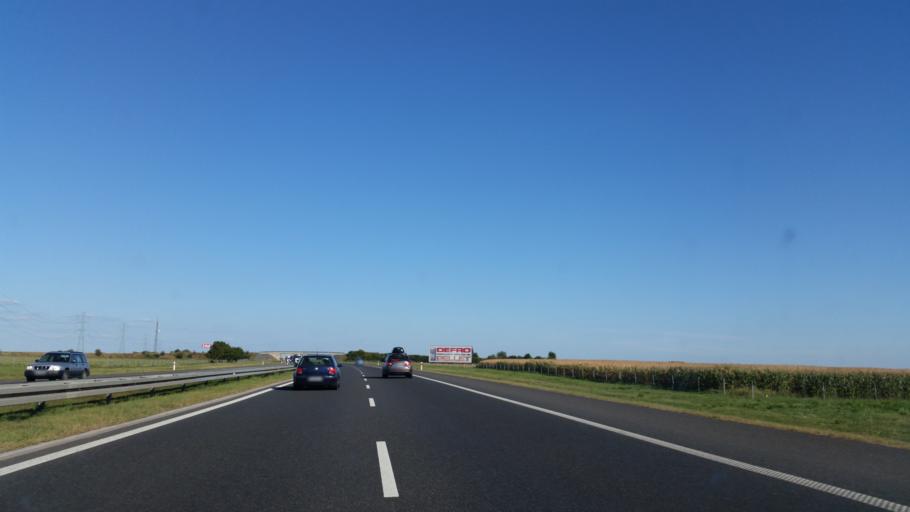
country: PL
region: Opole Voivodeship
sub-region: Powiat brzeski
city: Olszanka
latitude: 50.7400
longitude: 17.4640
